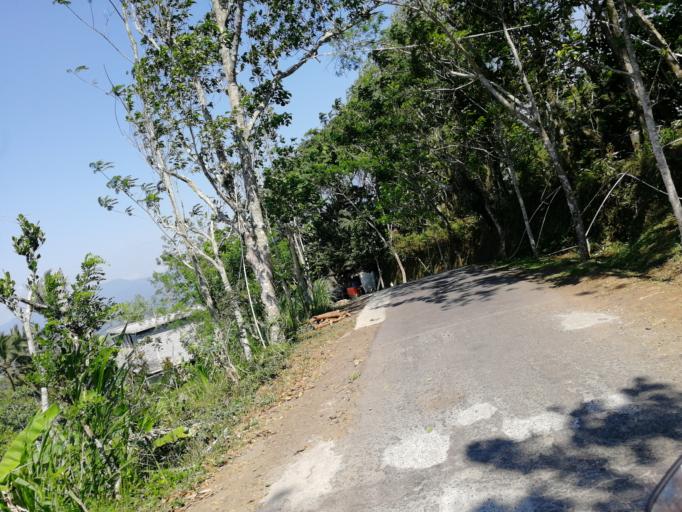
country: ID
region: Bali
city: Tiyingtali Kelod
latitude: -8.3918
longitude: 115.6322
